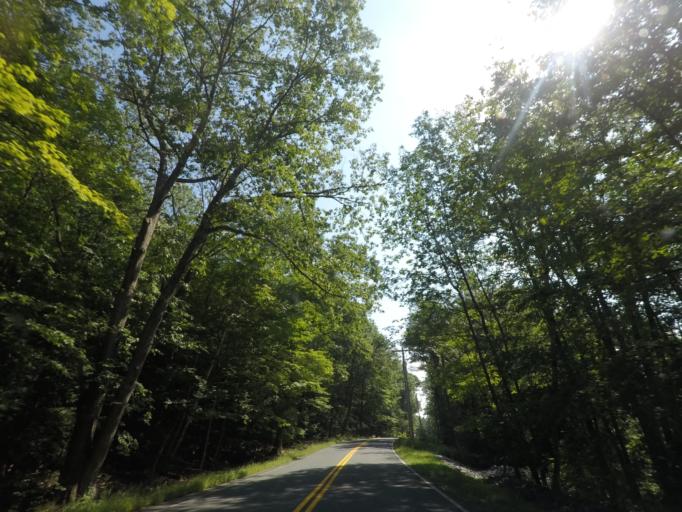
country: US
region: New York
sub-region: Rensselaer County
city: Poestenkill
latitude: 42.7278
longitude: -73.5097
